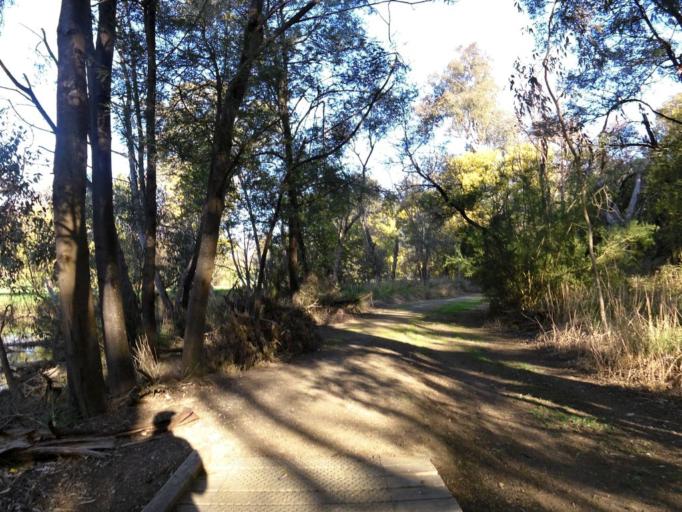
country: AU
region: Victoria
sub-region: Murrindindi
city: Alexandra
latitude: -37.2068
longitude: 145.4297
